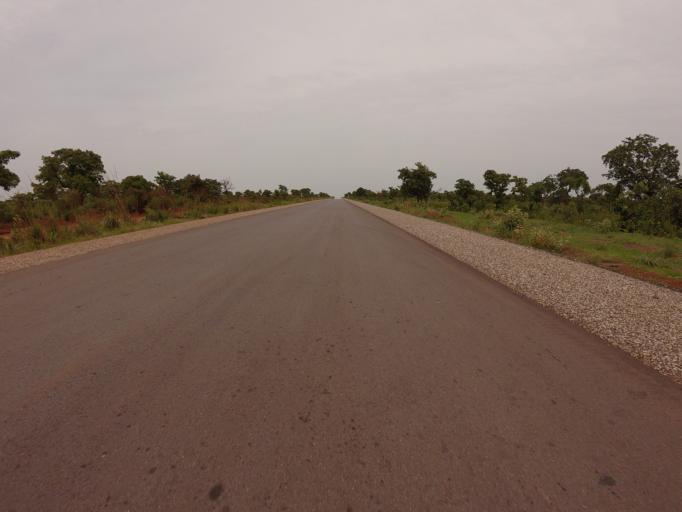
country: GH
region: Northern
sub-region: Yendi
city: Yendi
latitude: 8.9577
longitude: -0.0174
